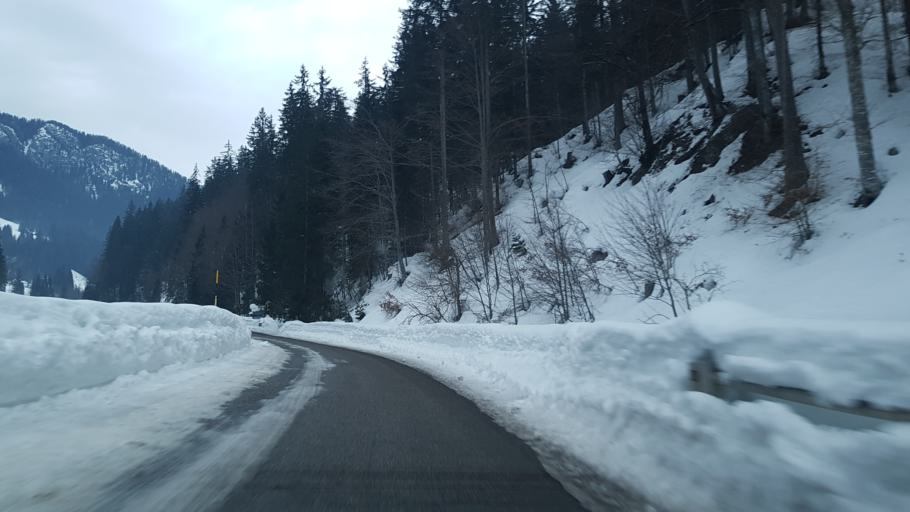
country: IT
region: Friuli Venezia Giulia
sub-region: Provincia di Udine
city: Malborghetto
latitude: 46.5361
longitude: 13.4735
